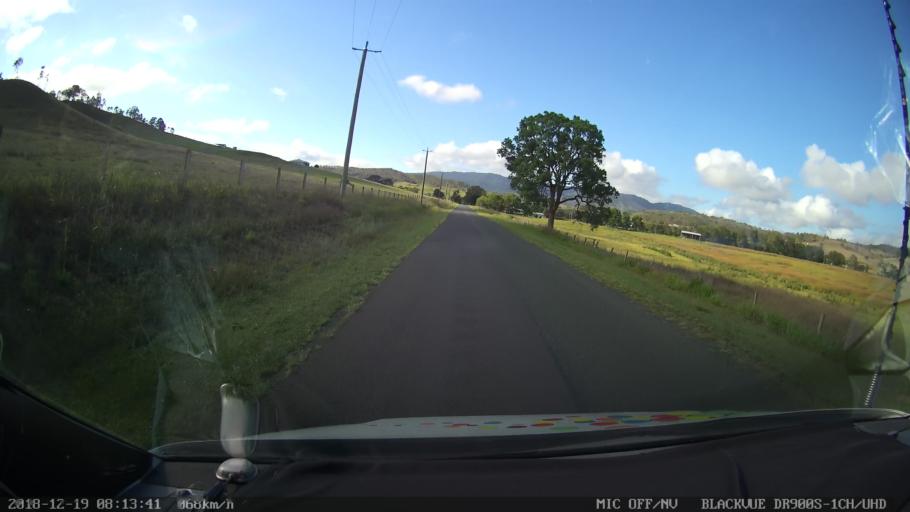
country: AU
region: Queensland
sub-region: Logan
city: Cedar Vale
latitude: -28.2411
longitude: 152.8903
